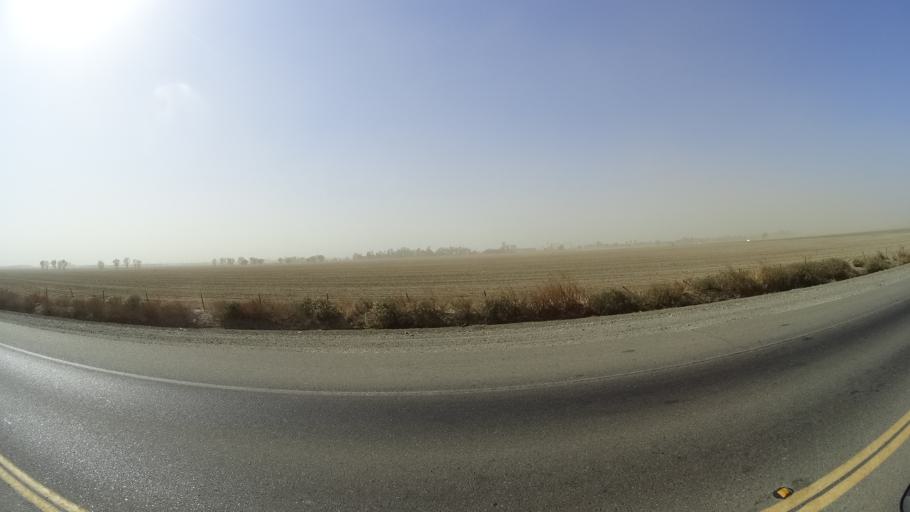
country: US
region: California
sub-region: Yolo County
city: Woodland
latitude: 38.7153
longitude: -121.7296
